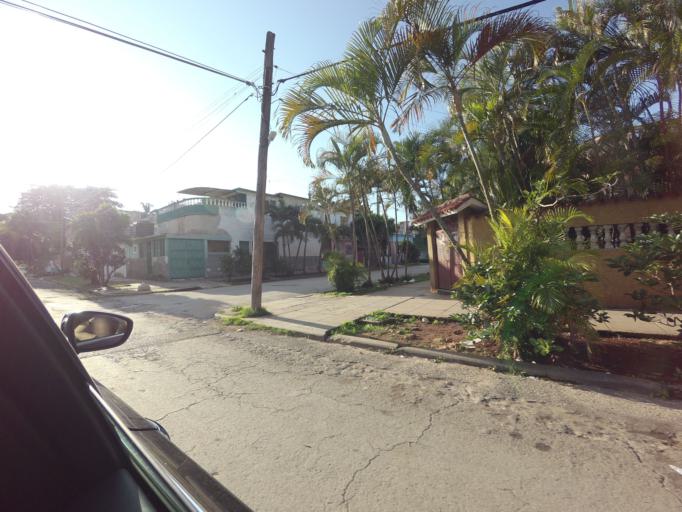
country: CU
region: La Habana
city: Havana
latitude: 23.1135
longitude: -82.4188
